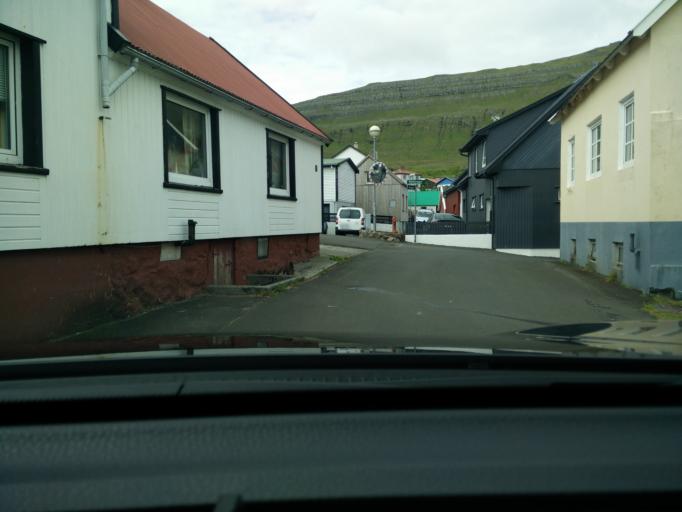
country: FO
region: Eysturoy
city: Eystur
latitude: 62.2096
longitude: -6.7018
